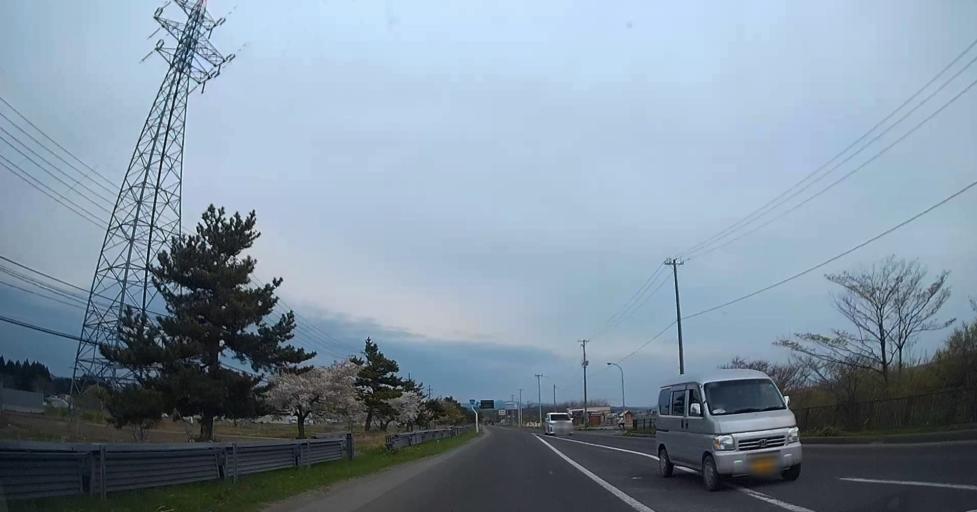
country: JP
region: Aomori
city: Aomori Shi
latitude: 40.8440
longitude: 140.6867
